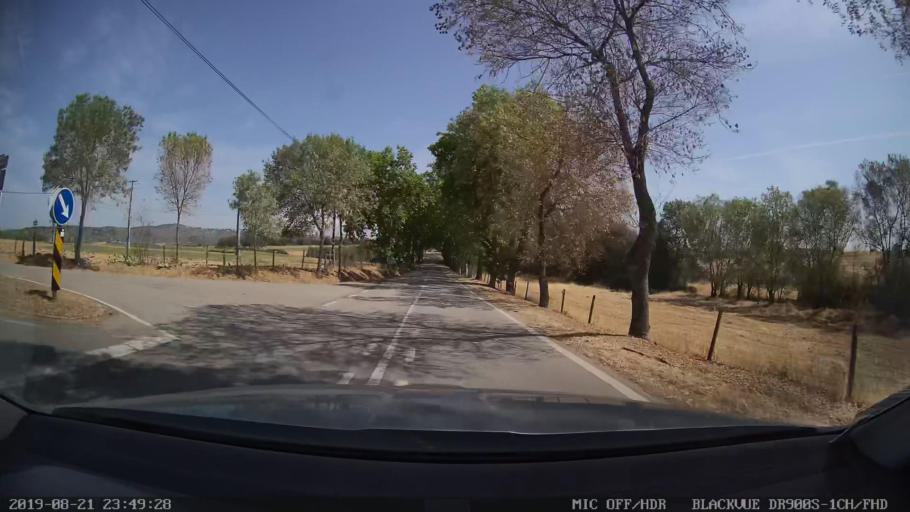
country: PT
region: Castelo Branco
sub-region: Idanha-A-Nova
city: Idanha-a-Nova
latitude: 39.8781
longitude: -7.2503
